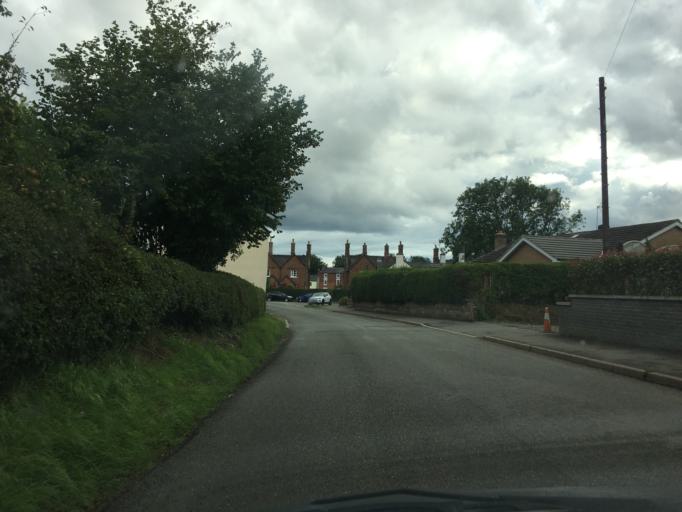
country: GB
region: England
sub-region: Leicestershire
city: Lutterworth
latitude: 52.4693
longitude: -1.2118
